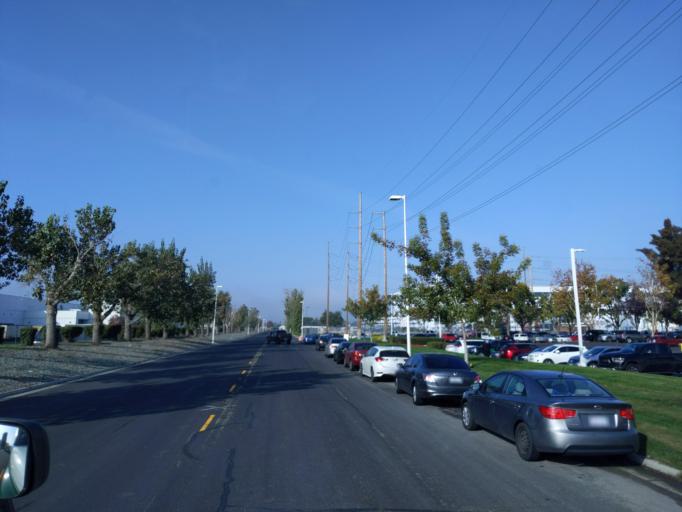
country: US
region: California
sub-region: San Joaquin County
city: Lathrop
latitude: 37.7977
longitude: -121.2930
